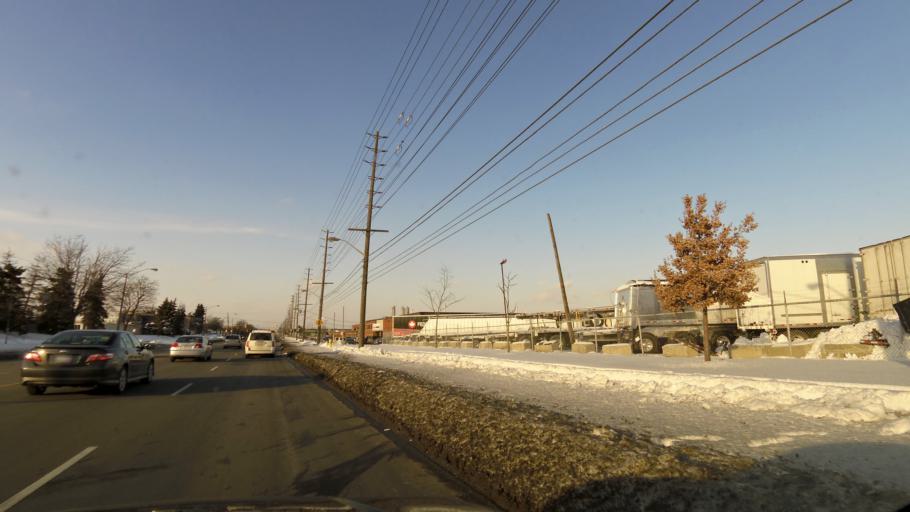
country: CA
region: Ontario
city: Etobicoke
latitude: 43.7029
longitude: -79.5760
